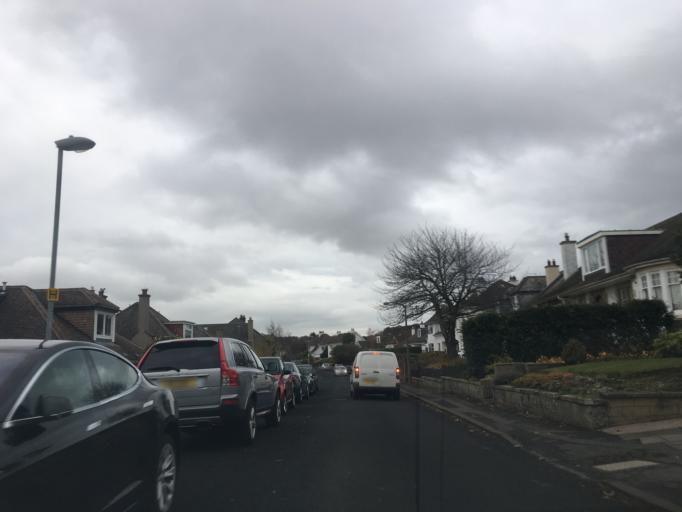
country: GB
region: Scotland
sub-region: Edinburgh
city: Colinton
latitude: 55.9077
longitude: -3.2155
